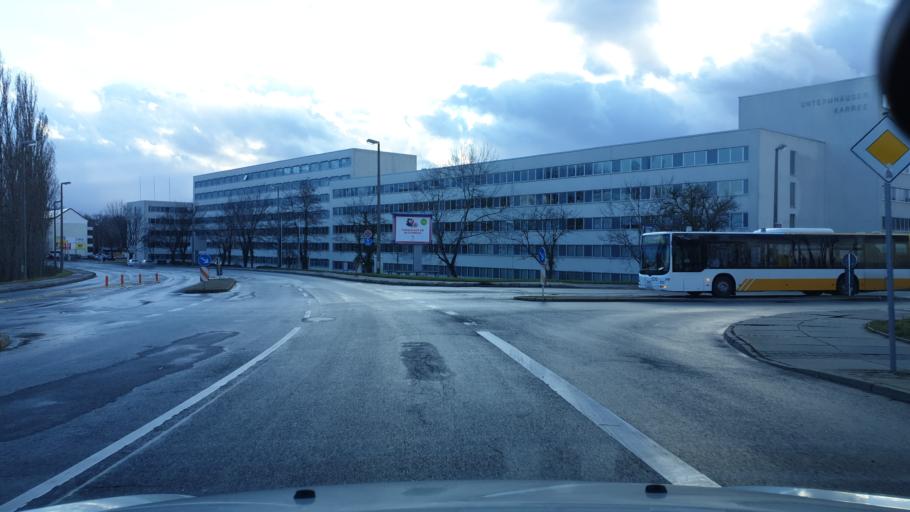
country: DE
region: Thuringia
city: Gera
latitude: 50.8896
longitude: 12.0743
